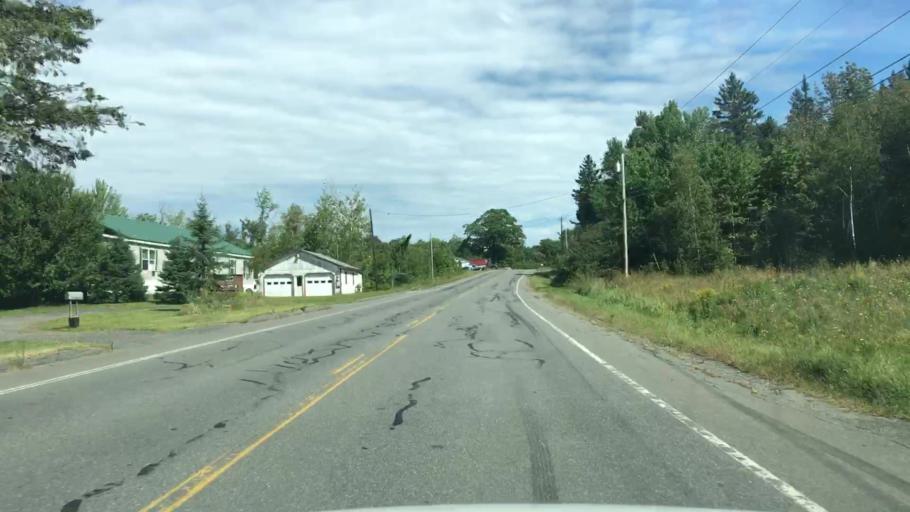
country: US
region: Maine
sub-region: Penobscot County
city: Garland
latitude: 45.0809
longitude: -69.2296
